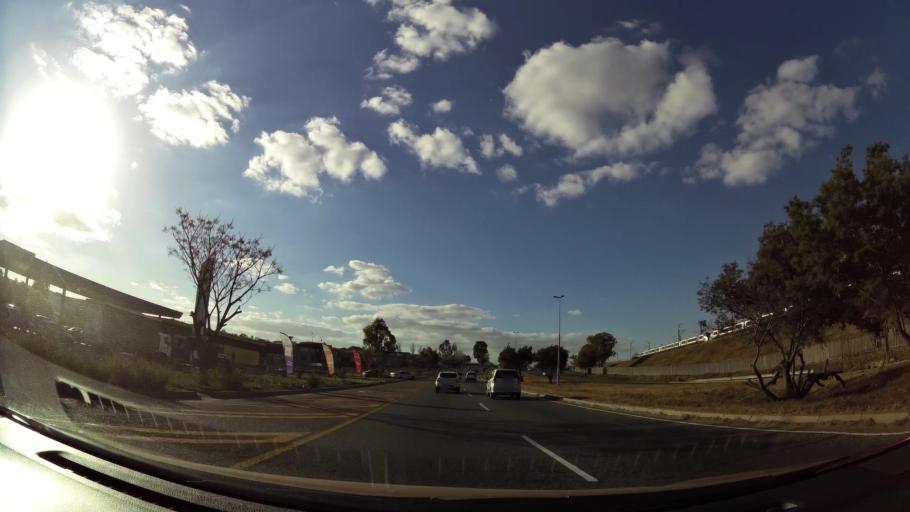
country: ZA
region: Gauteng
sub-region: City of Johannesburg Metropolitan Municipality
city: Midrand
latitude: -25.9860
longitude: 28.1318
